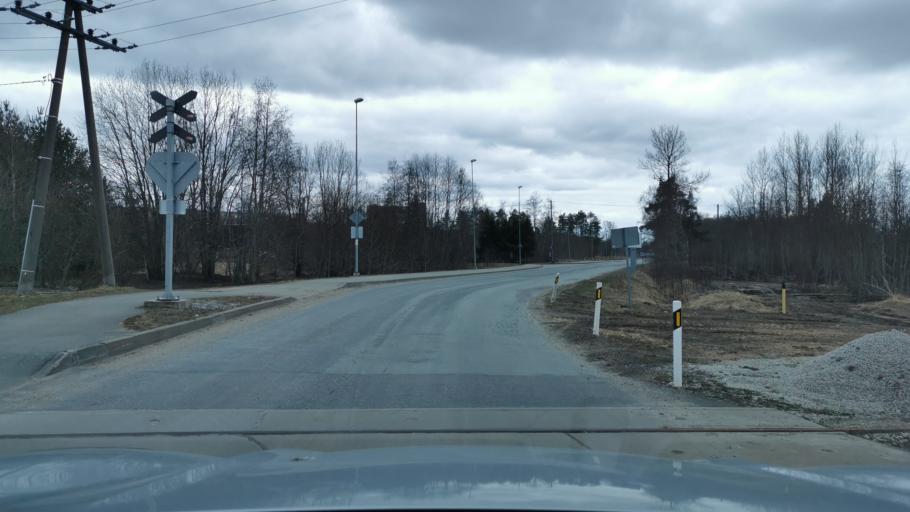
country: EE
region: Ida-Virumaa
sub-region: Puessi linn
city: Pussi
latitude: 59.3583
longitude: 27.0405
